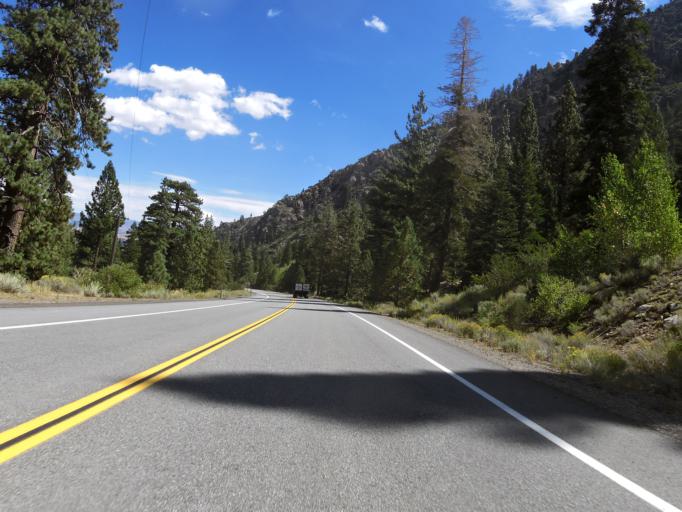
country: US
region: Nevada
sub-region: Douglas County
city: Gardnerville Ranchos
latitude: 38.7639
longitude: -119.8564
